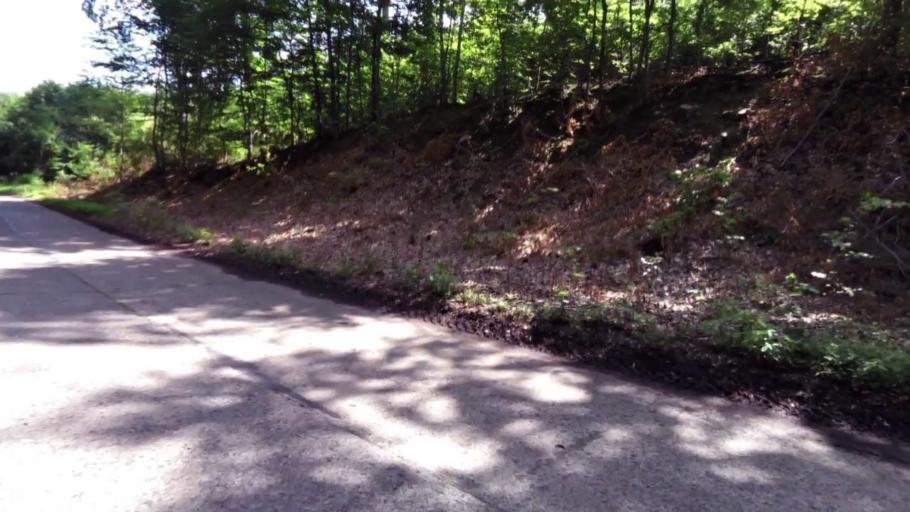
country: PL
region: West Pomeranian Voivodeship
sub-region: Powiat stargardzki
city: Insko
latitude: 53.3915
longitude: 15.5022
